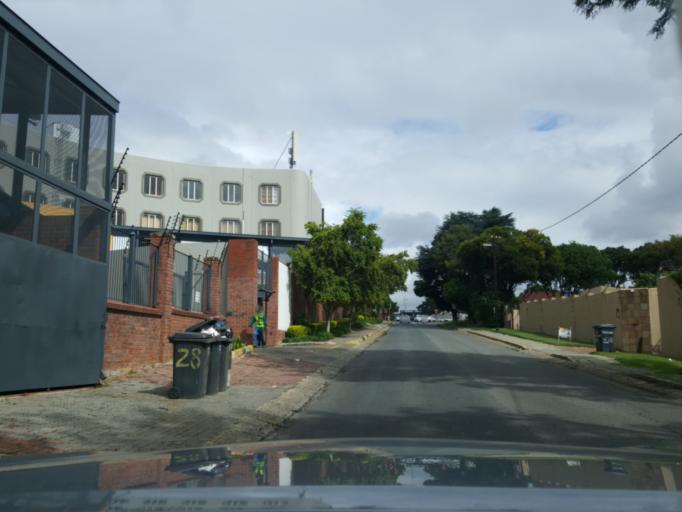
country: ZA
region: Gauteng
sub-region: City of Johannesburg Metropolitan Municipality
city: Johannesburg
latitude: -26.1134
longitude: 27.9992
